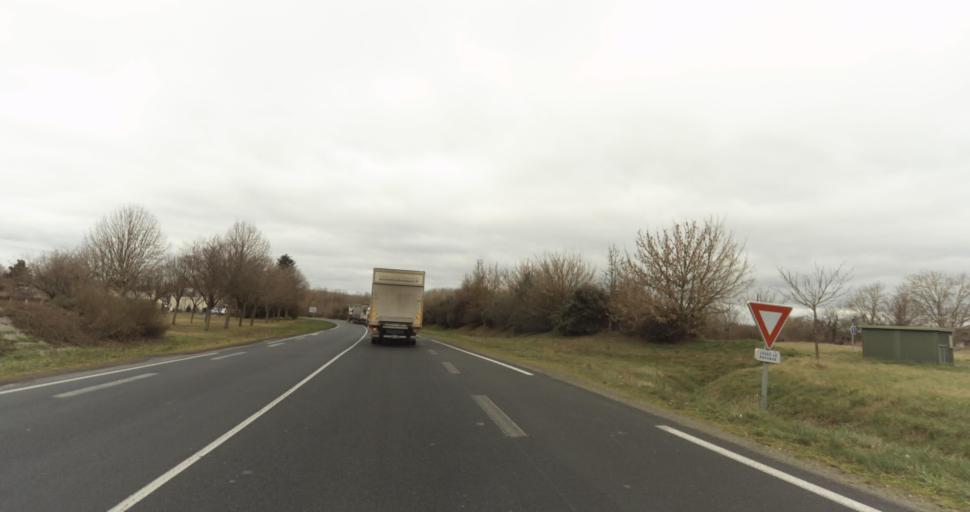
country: FR
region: Pays de la Loire
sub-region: Departement de Maine-et-Loire
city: Jumelles
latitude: 47.3798
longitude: -0.1026
